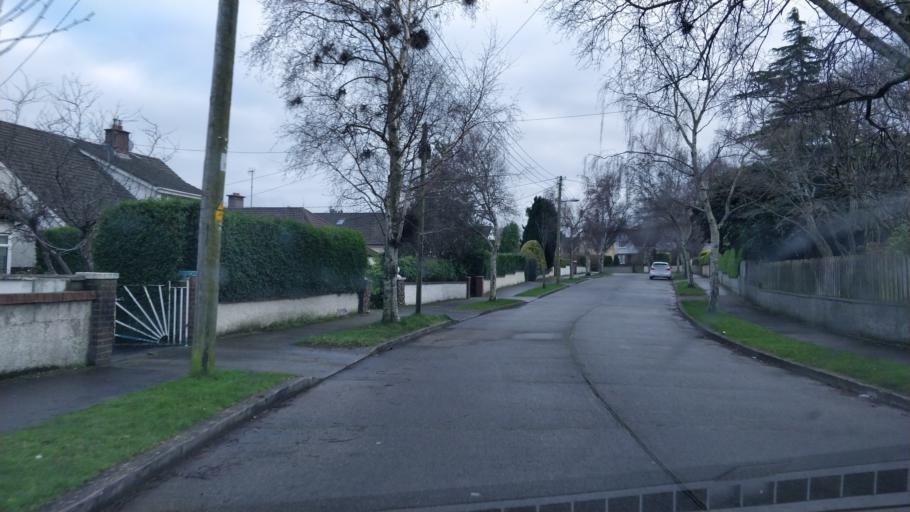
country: IE
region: Leinster
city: Foxrock
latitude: 53.2799
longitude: -6.1777
